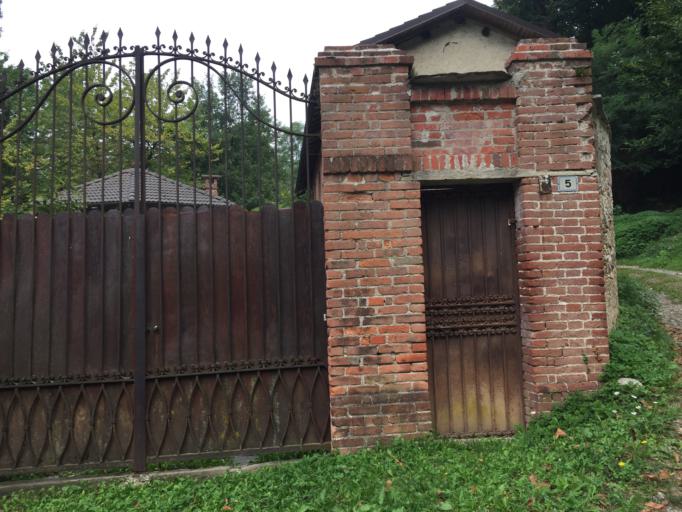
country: IT
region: Piedmont
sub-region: Provincia di Cuneo
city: Chiusa di Pesio
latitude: 44.3216
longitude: 7.6857
